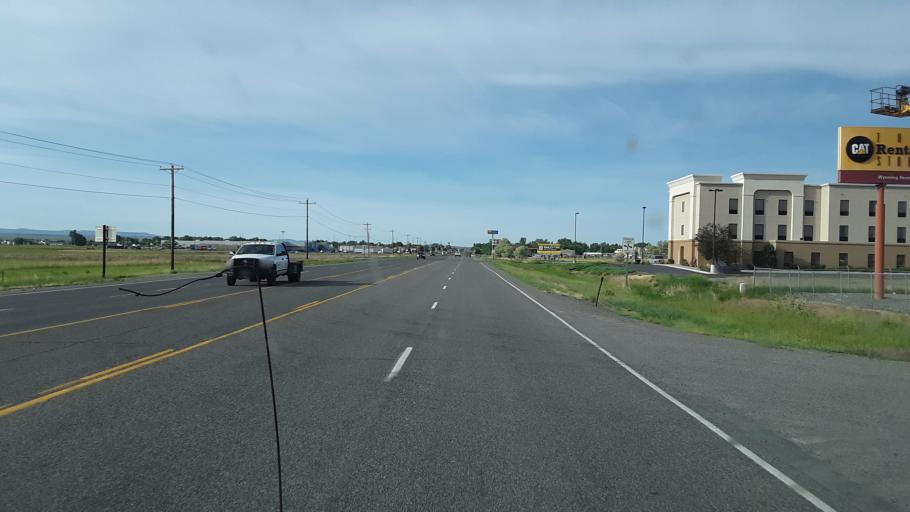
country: US
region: Wyoming
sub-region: Fremont County
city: Riverton
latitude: 43.0492
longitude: -108.3808
